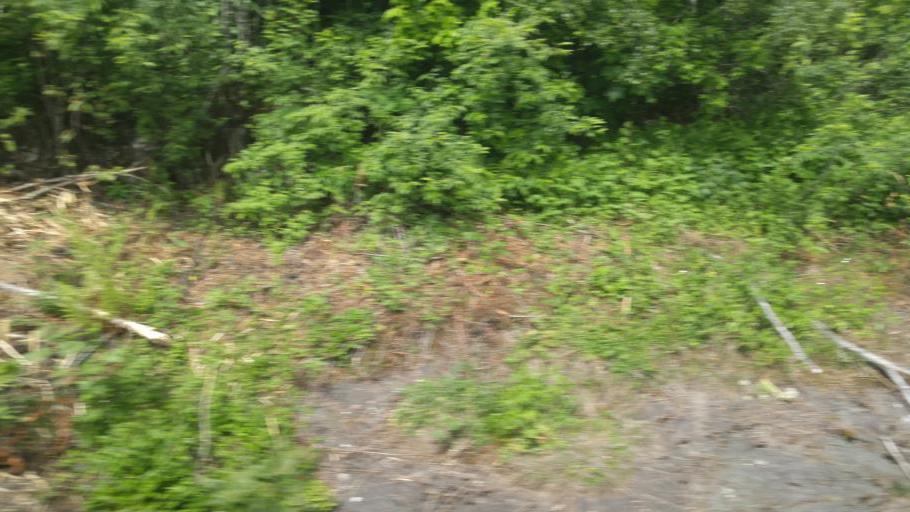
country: NO
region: Sor-Trondelag
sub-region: Trondheim
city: Trondheim
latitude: 63.3968
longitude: 10.3841
